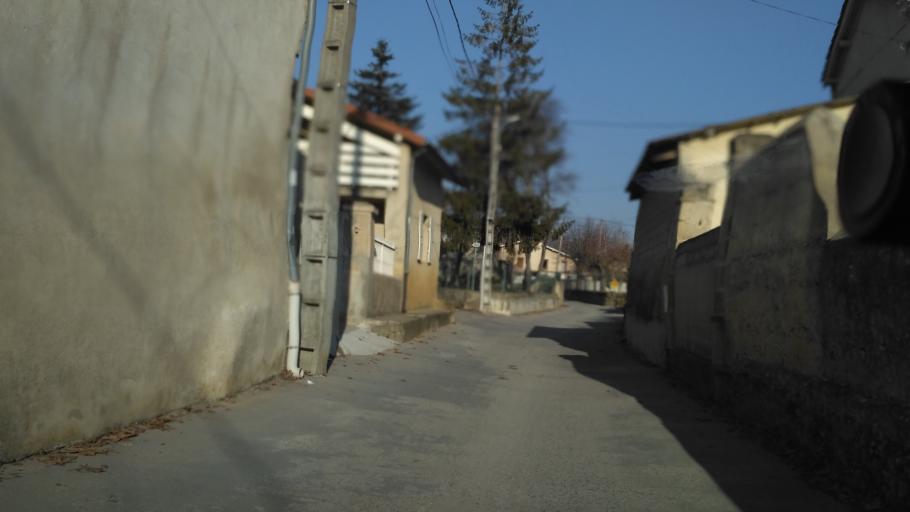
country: FR
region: Rhone-Alpes
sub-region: Departement de la Drome
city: Clerieux
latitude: 45.0757
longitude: 4.9595
